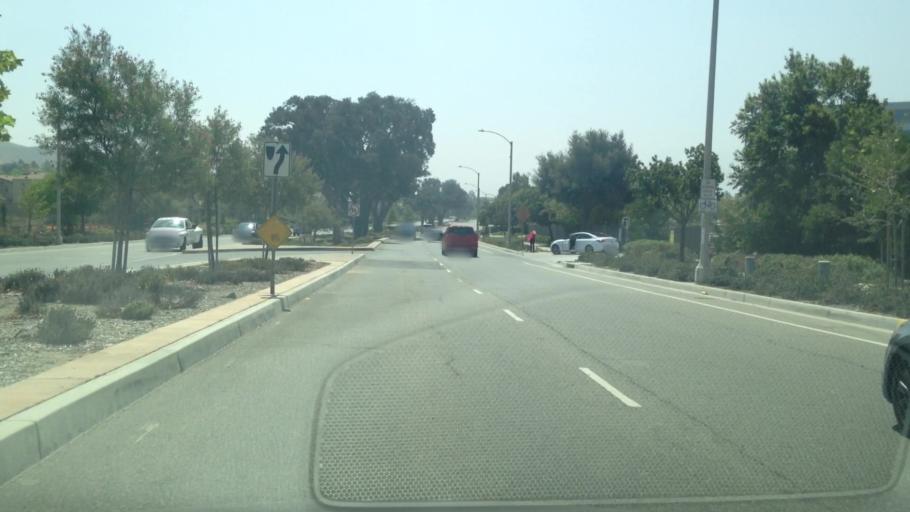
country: US
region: California
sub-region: Riverside County
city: El Cerrito
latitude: 33.8212
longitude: -117.5087
